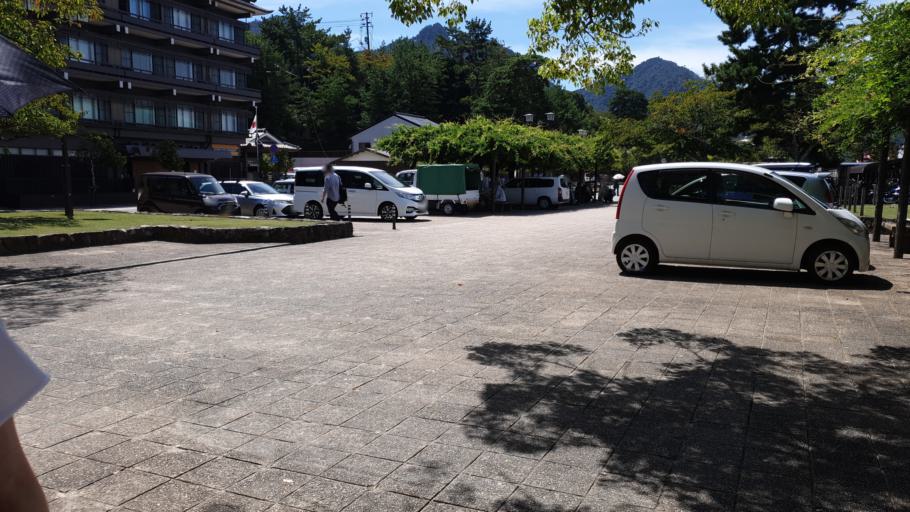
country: JP
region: Hiroshima
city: Miyajima
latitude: 34.3026
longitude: 132.3231
